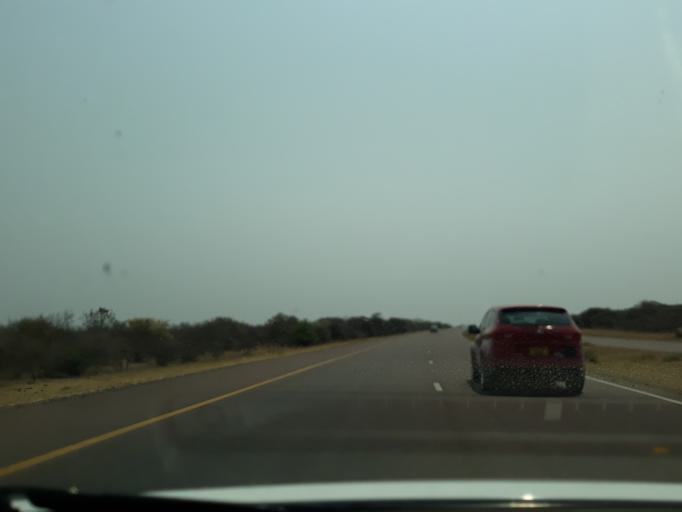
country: BW
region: Kgatleng
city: Bokaa
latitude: -24.4217
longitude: 26.0477
